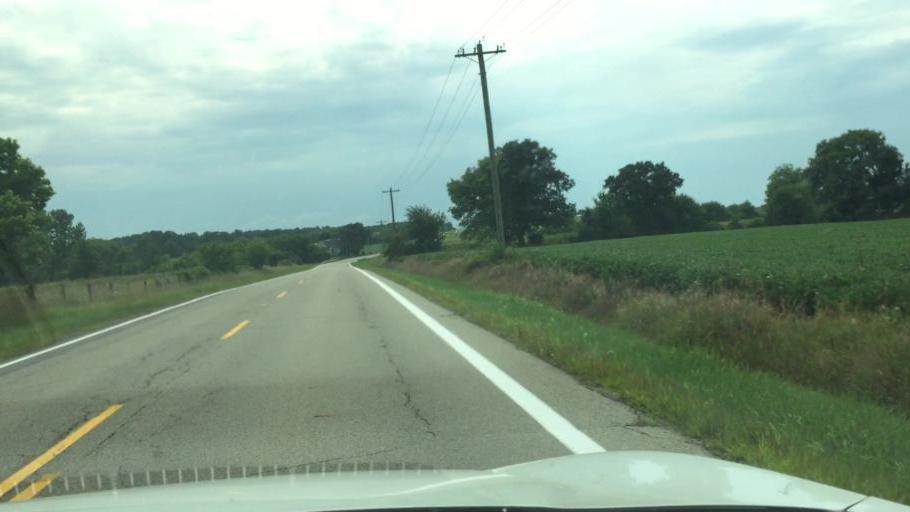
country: US
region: Ohio
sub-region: Champaign County
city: Mechanicsburg
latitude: 40.1003
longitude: -83.5480
